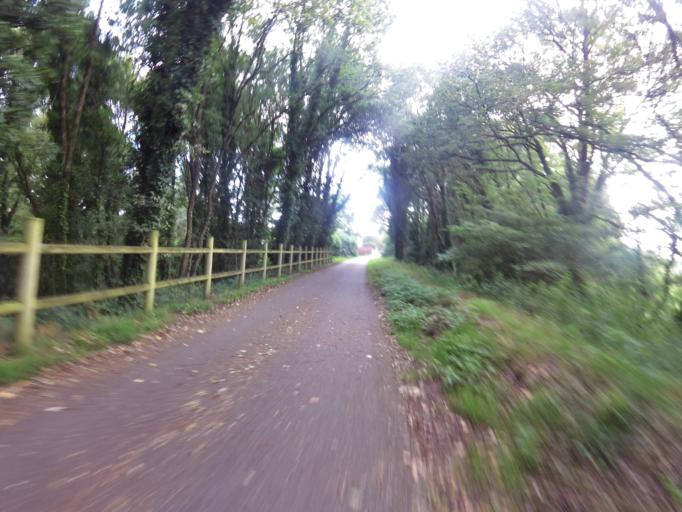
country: FR
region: Brittany
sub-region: Departement du Morbihan
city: Ploermel
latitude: 47.9183
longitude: -2.4276
